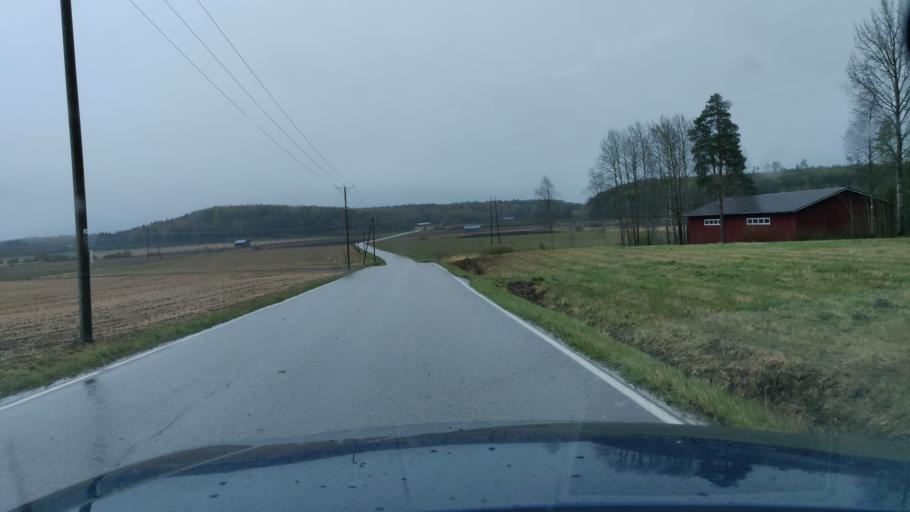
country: FI
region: Uusimaa
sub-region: Helsinki
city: Nurmijaervi
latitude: 60.4775
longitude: 24.7638
